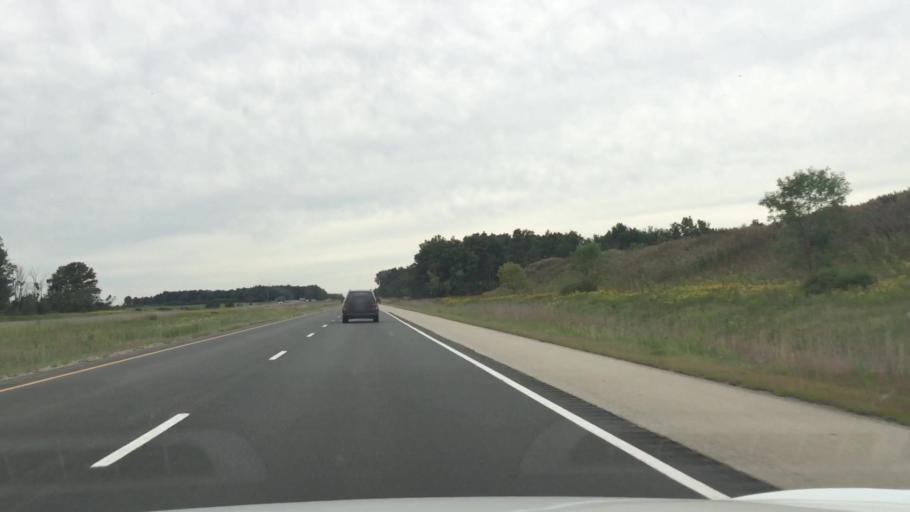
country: CA
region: Ontario
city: Lambton Shores
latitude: 42.9922
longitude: -81.8953
